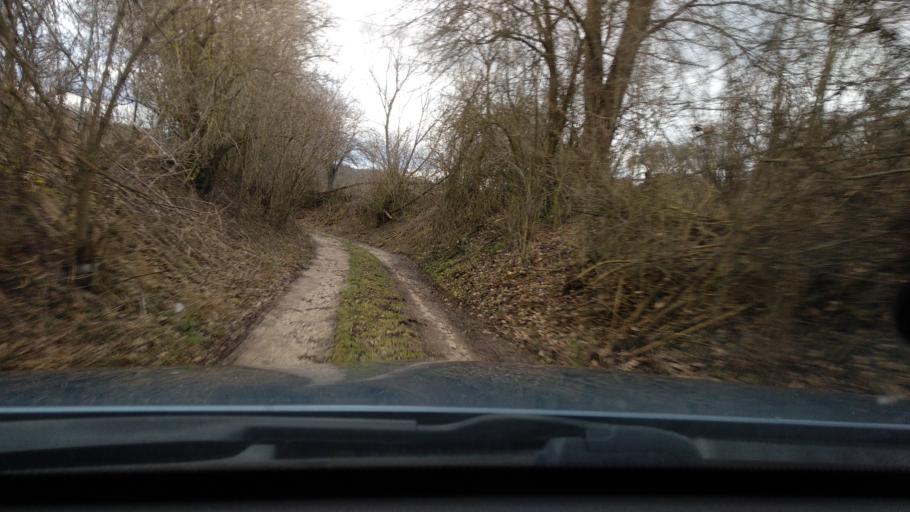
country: SK
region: Nitriansky
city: Trencianske Teplice
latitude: 48.8391
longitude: 18.1806
